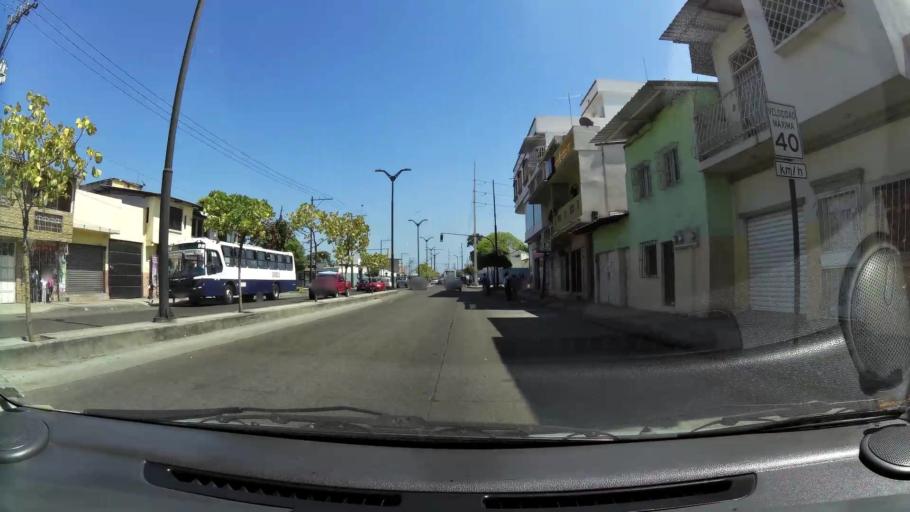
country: EC
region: Guayas
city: Guayaquil
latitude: -2.2152
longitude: -79.9352
